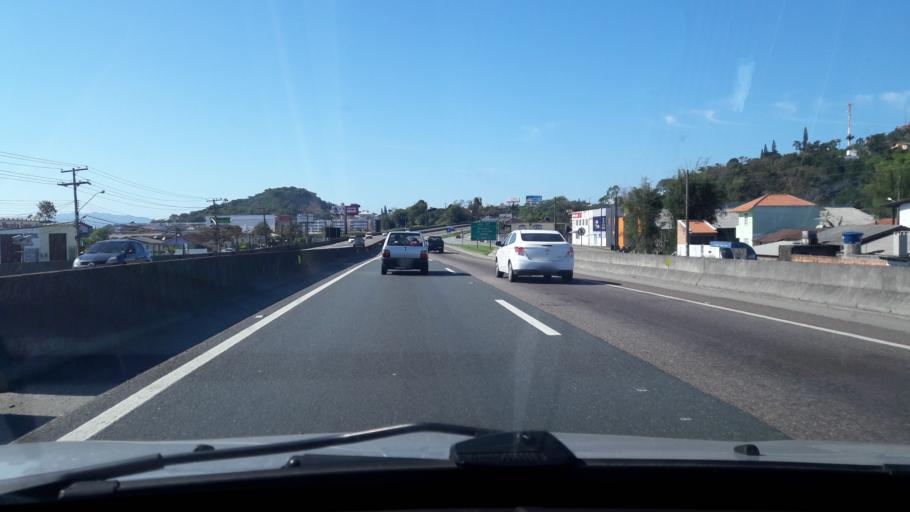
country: BR
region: Santa Catarina
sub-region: Biguacu
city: Biguacu
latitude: -27.5117
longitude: -48.6425
